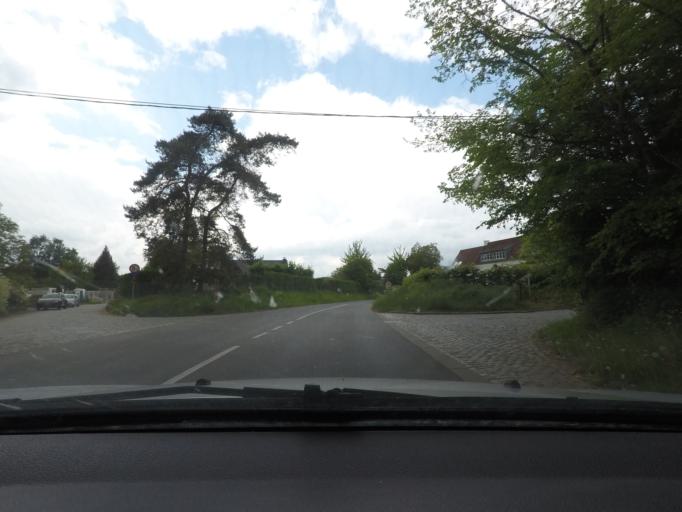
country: BE
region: Wallonia
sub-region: Province du Hainaut
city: Basse Lasne
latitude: 50.6640
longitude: 4.4950
